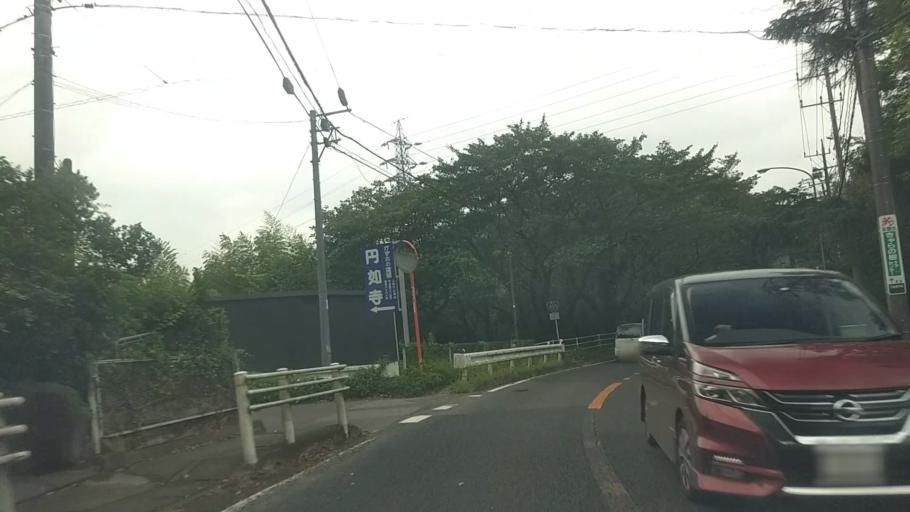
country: JP
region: Chiba
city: Kisarazu
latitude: 35.3000
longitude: 140.0746
